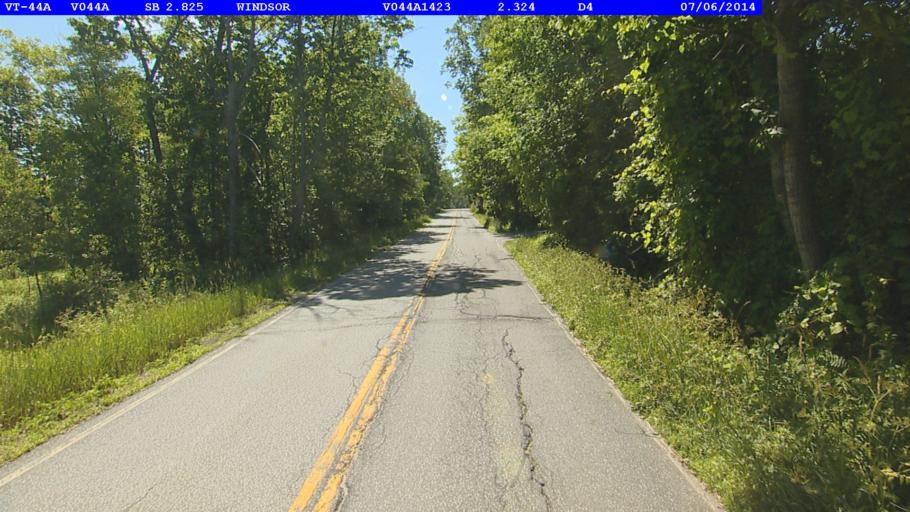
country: US
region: Vermont
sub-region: Windsor County
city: Windsor
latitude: 43.4574
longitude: -72.4221
